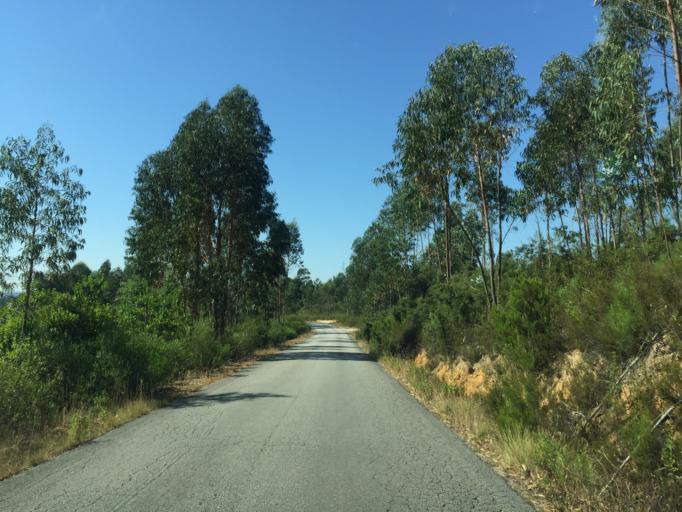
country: PT
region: Santarem
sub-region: Tomar
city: Tomar
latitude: 39.5628
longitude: -8.3213
